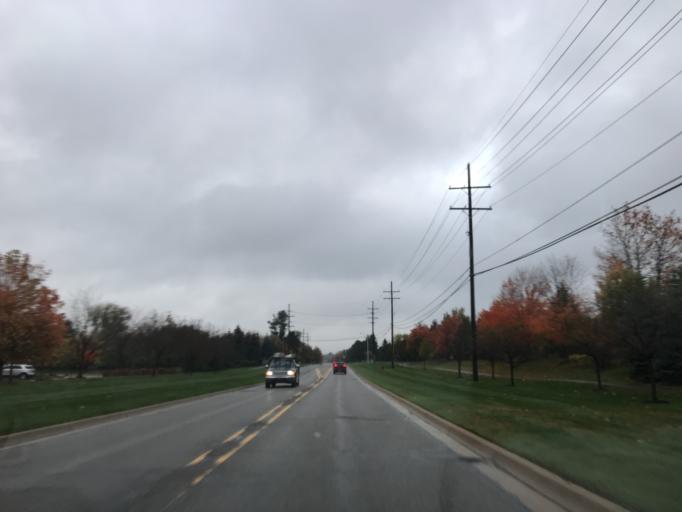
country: US
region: Michigan
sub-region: Oakland County
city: Wixom
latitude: 42.4703
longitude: -83.5341
